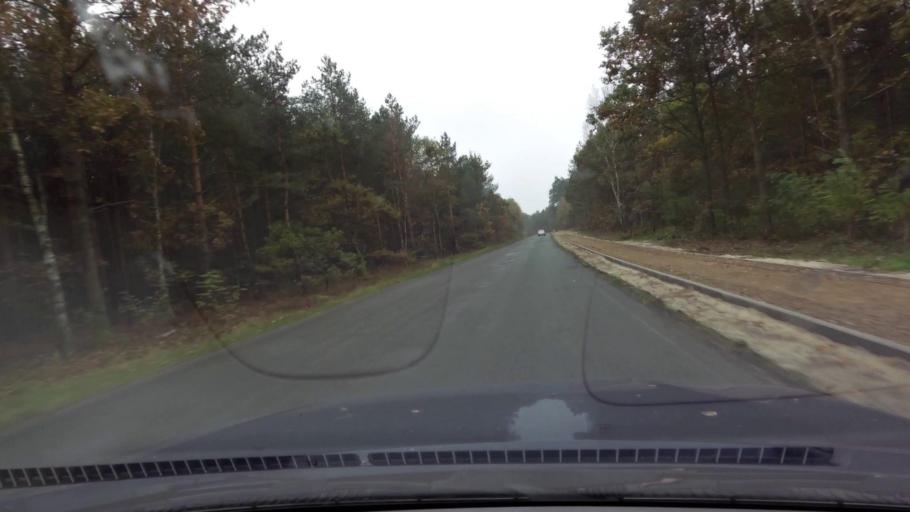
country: PL
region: West Pomeranian Voivodeship
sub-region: Powiat goleniowski
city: Goleniow
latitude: 53.5401
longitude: 14.7675
